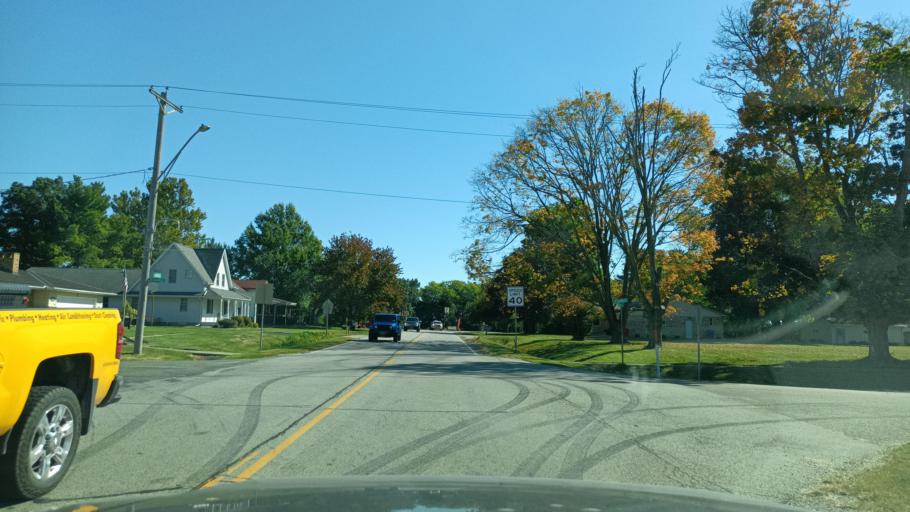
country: US
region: Illinois
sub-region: Peoria County
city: Elmwood
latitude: 40.8388
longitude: -89.8816
